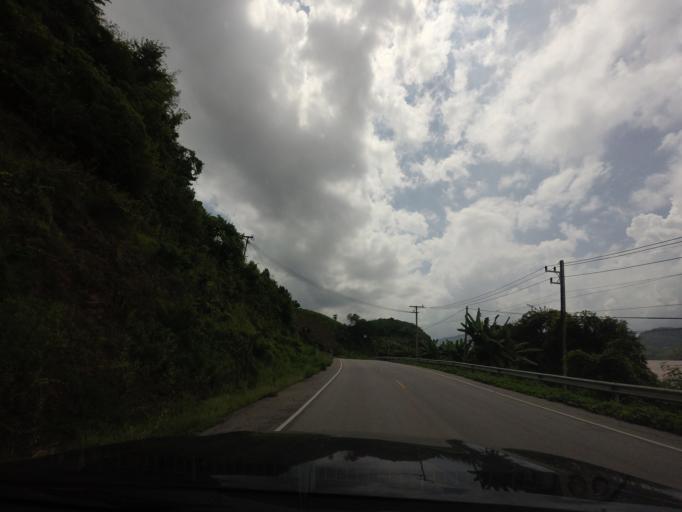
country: TH
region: Loei
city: Pak Chom
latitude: 18.0486
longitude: 101.7748
